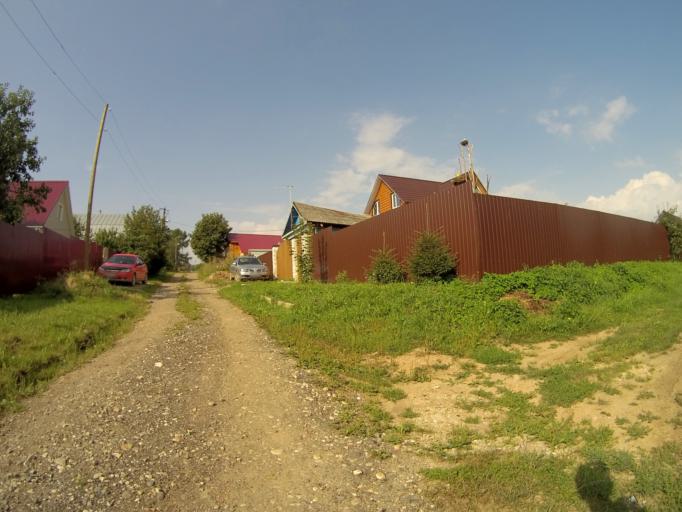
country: RU
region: Vladimir
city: Vladimir
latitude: 56.1326
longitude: 40.2976
